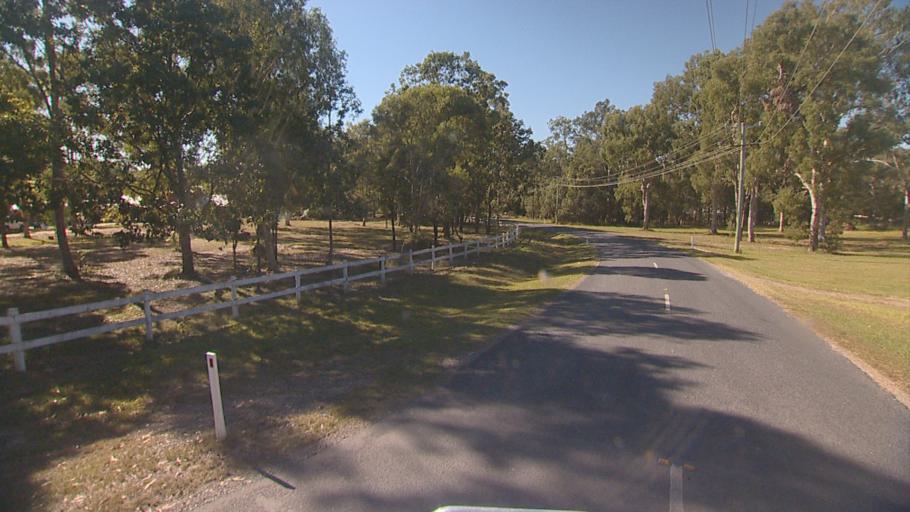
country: AU
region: Queensland
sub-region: Logan
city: Logan Reserve
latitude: -27.7362
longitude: 153.1223
